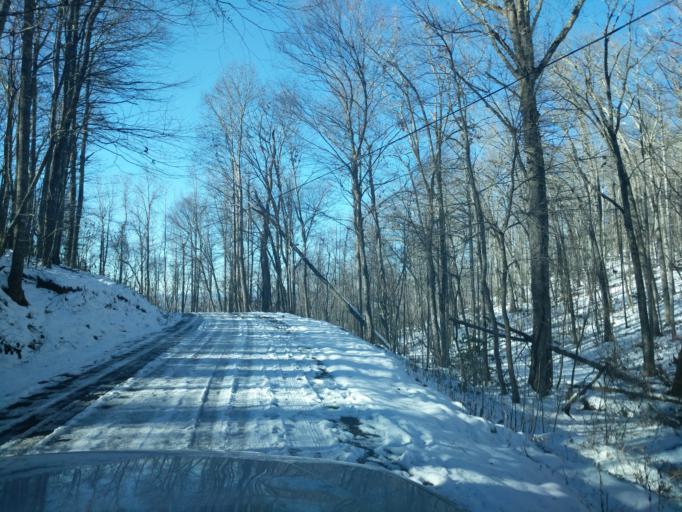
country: US
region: Georgia
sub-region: Towns County
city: Hiawassee
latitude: 34.9556
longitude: -83.7300
